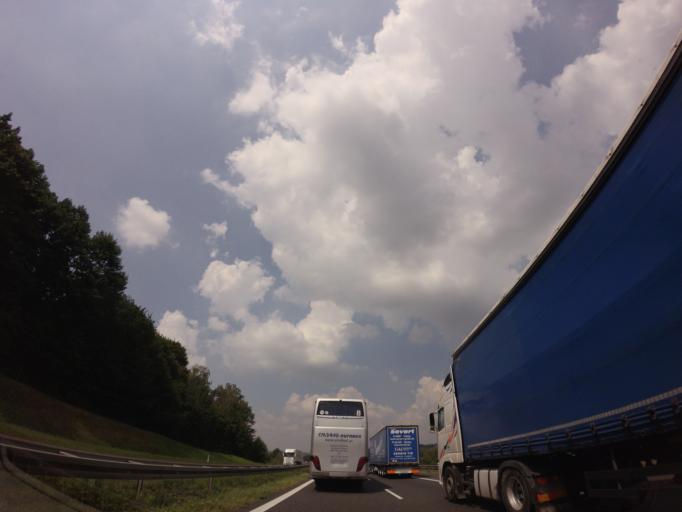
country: PL
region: Silesian Voivodeship
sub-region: Powiat gliwicki
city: Rudziniec
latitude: 50.3849
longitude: 18.4598
